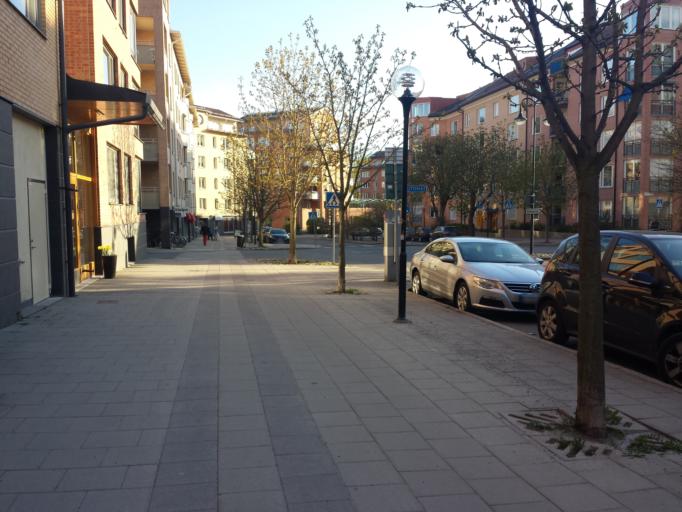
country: SE
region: Stockholm
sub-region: Solna Kommun
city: Solna
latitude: 59.3687
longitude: 18.0162
